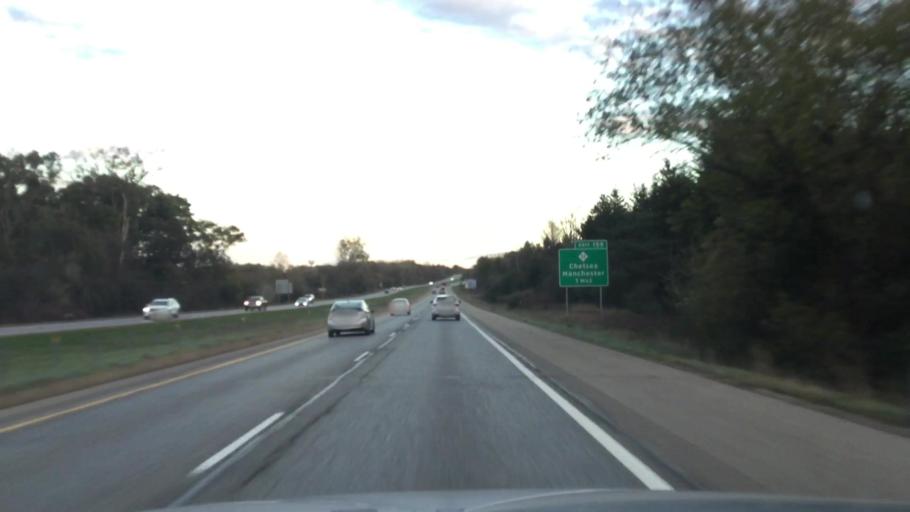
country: US
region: Michigan
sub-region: Washtenaw County
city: Chelsea
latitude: 42.2936
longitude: -84.0499
